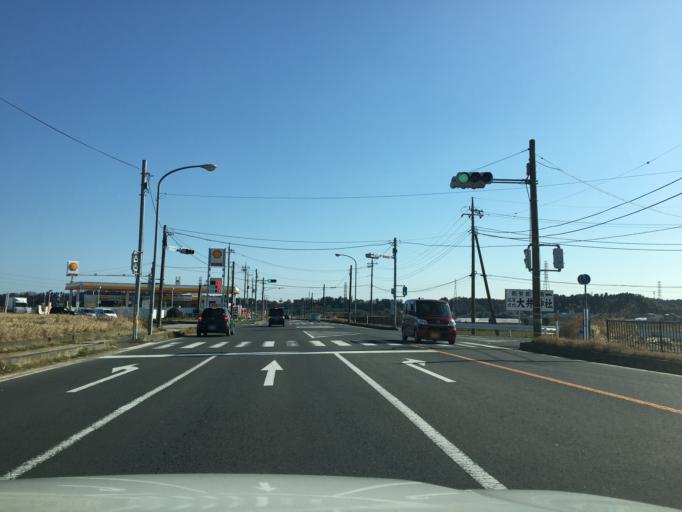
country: JP
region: Ibaraki
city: Mito-shi
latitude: 36.4244
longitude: 140.4221
